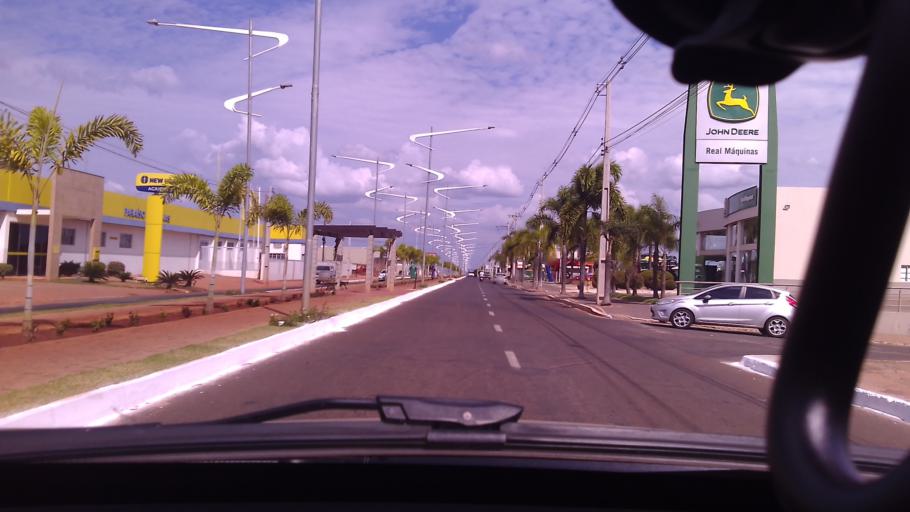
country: BR
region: Goias
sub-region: Mineiros
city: Mineiros
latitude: -17.5404
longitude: -52.5394
